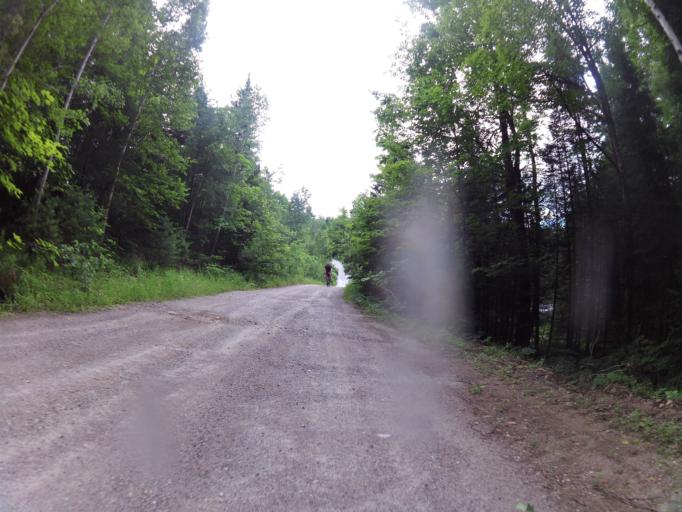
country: CA
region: Ontario
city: Perth
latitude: 45.0092
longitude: -76.5904
